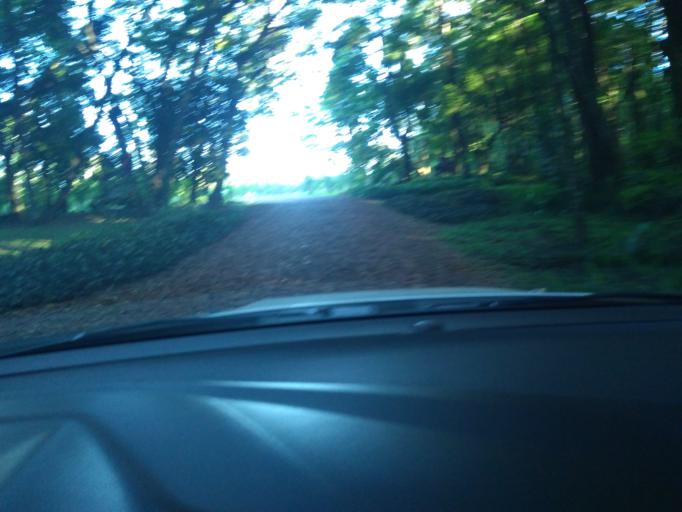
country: AR
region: Misiones
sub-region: Departamento de Obera
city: Obera
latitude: -27.4693
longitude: -55.0854
